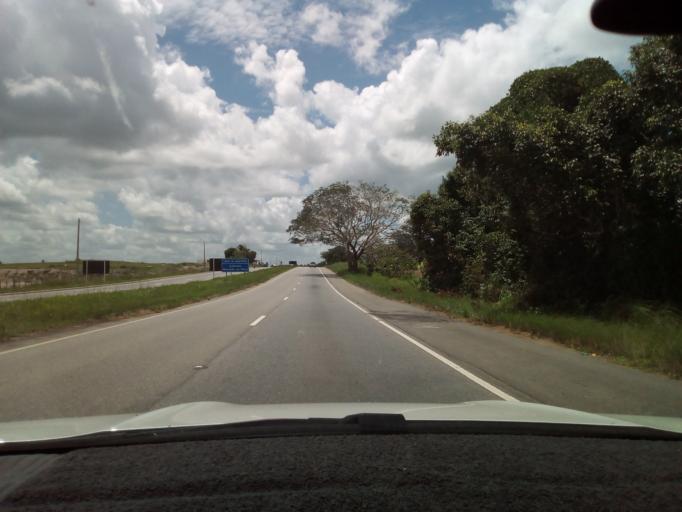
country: BR
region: Paraiba
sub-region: Pilar
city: Pilar
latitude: -7.1891
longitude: -35.2781
